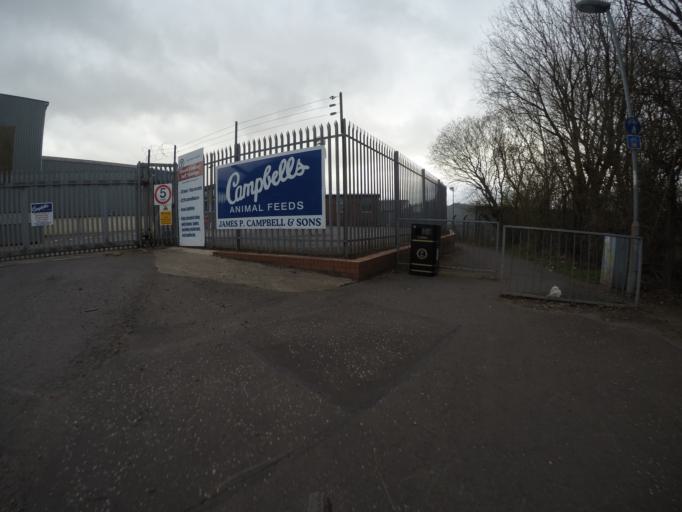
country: GB
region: Scotland
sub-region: East Ayrshire
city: Kilmarnock
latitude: 55.6159
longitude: -4.5058
